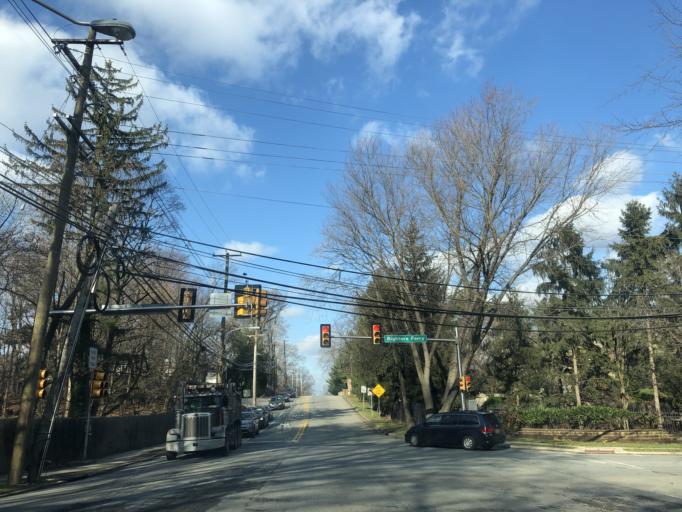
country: US
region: Pennsylvania
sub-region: Montgomery County
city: Bala-Cynwyd
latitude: 40.0079
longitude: -75.2236
